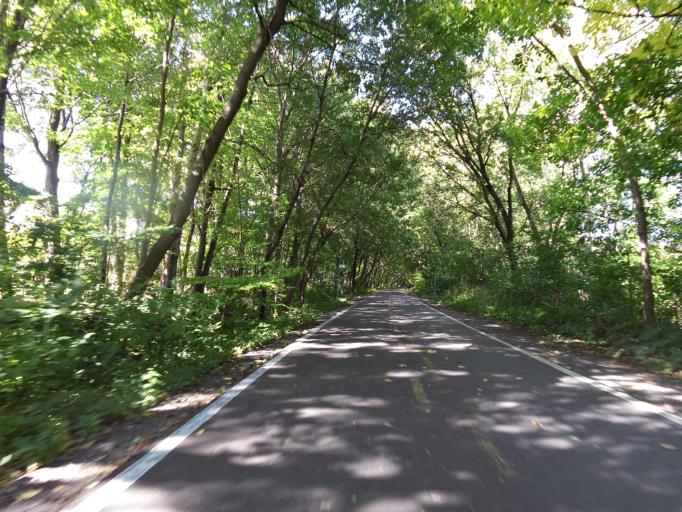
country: CA
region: Ontario
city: Bourget
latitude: 45.2627
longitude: -75.3644
